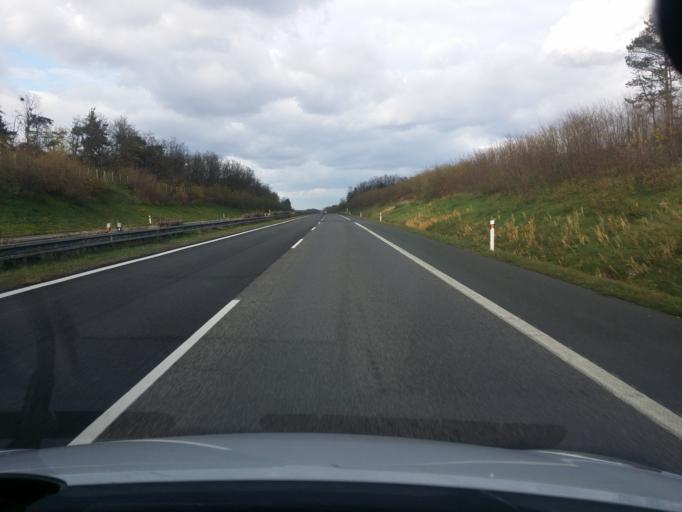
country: AT
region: Lower Austria
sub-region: Politischer Bezirk Ganserndorf
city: Drosing
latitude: 48.5811
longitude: 17.0161
